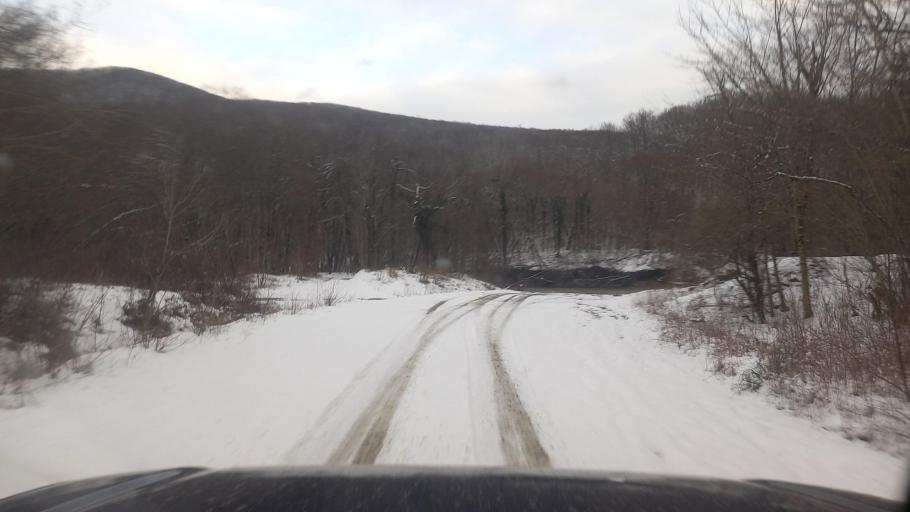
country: RU
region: Krasnodarskiy
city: Smolenskaya
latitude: 44.6580
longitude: 38.7682
